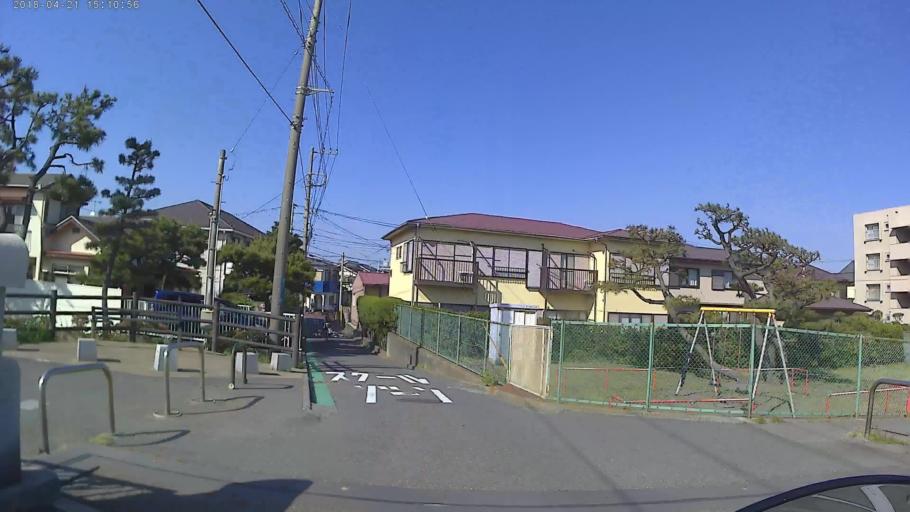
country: JP
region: Kanagawa
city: Fujisawa
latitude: 35.3186
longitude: 139.4651
